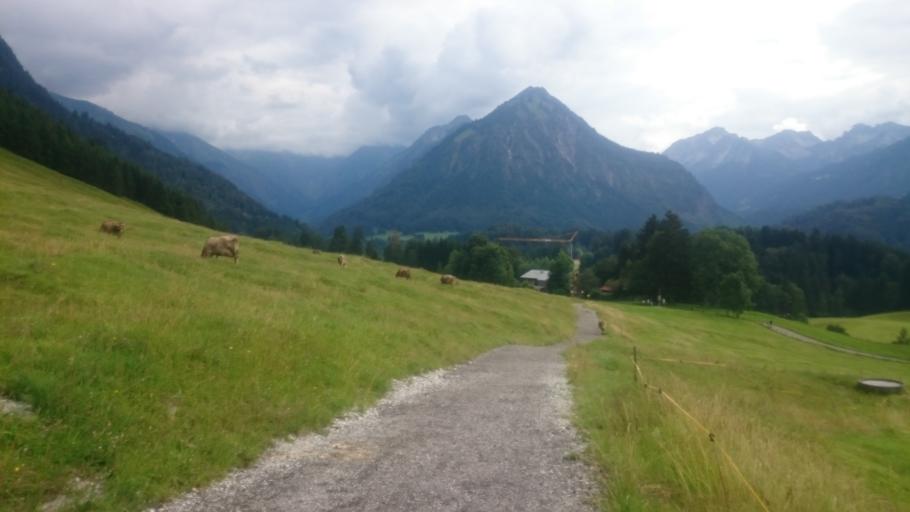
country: DE
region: Bavaria
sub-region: Swabia
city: Oberstdorf
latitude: 47.4014
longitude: 10.2946
